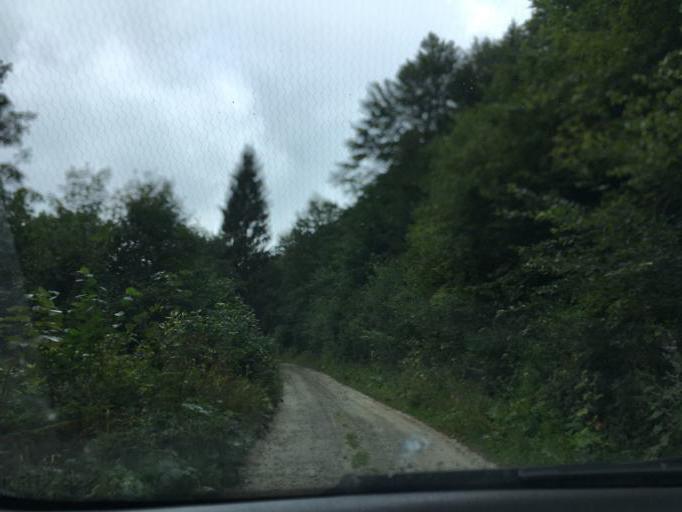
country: PL
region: Subcarpathian Voivodeship
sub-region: Powiat bieszczadzki
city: Lutowiska
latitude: 49.1888
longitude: 22.6150
